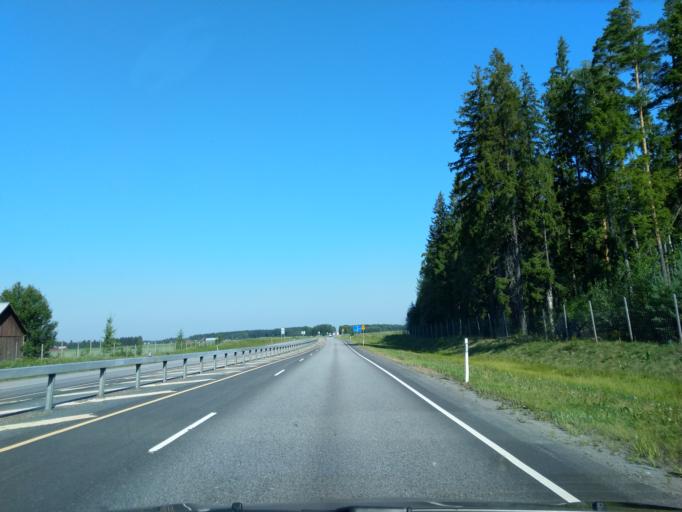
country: FI
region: Varsinais-Suomi
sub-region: Loimaa
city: Alastaro
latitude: 61.0586
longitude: 22.9446
